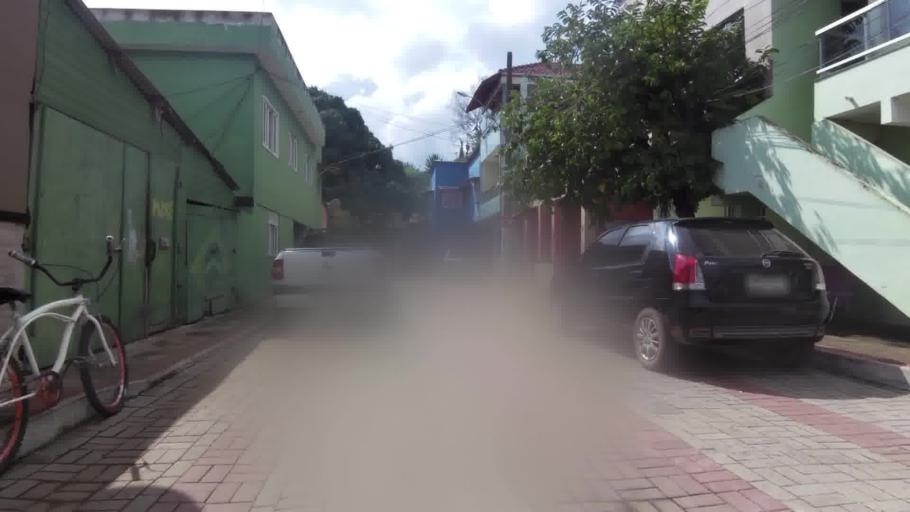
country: BR
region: Espirito Santo
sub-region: Piuma
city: Piuma
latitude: -20.8027
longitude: -40.6544
